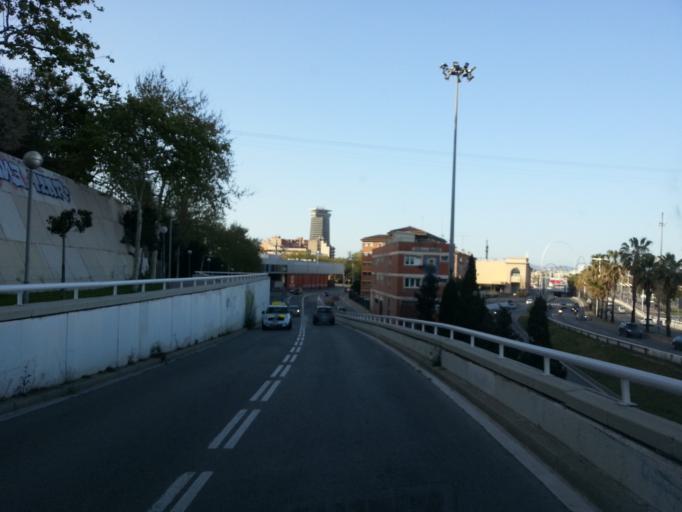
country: ES
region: Catalonia
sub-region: Provincia de Barcelona
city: Ciutat Vella
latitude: 41.3694
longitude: 2.1735
